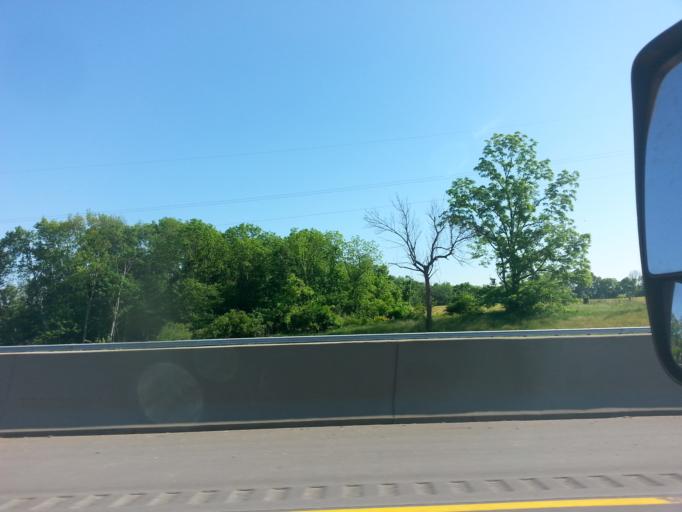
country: US
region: Kentucky
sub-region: Shelby County
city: Simpsonville
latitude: 38.2024
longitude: -85.3150
